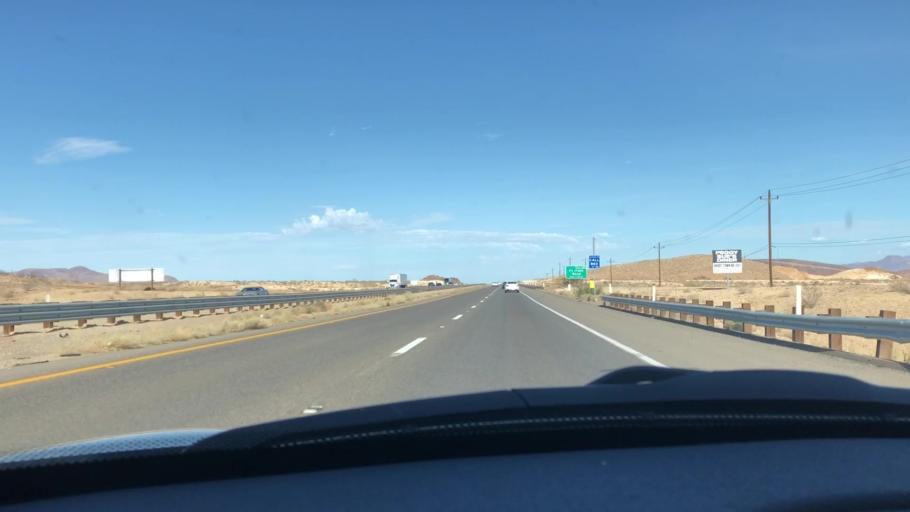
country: US
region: California
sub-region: San Bernardino County
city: Barstow
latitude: 34.9047
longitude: -116.9451
